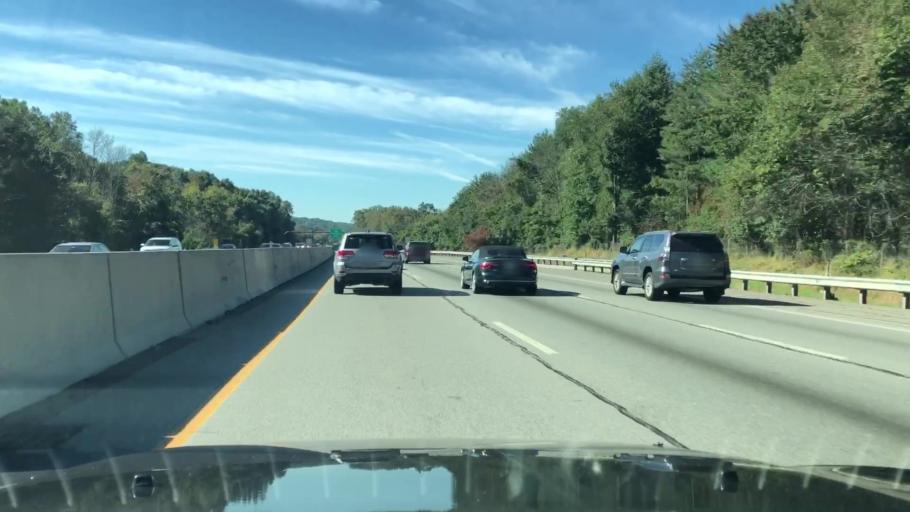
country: US
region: Pennsylvania
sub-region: Montgomery County
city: Dresher
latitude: 40.1499
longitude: -75.1467
